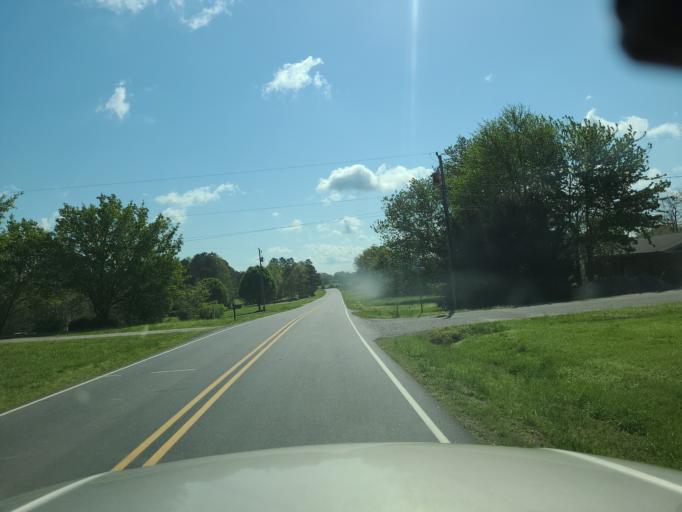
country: US
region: North Carolina
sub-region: Rutherford County
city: Spindale
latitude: 35.2968
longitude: -81.9305
